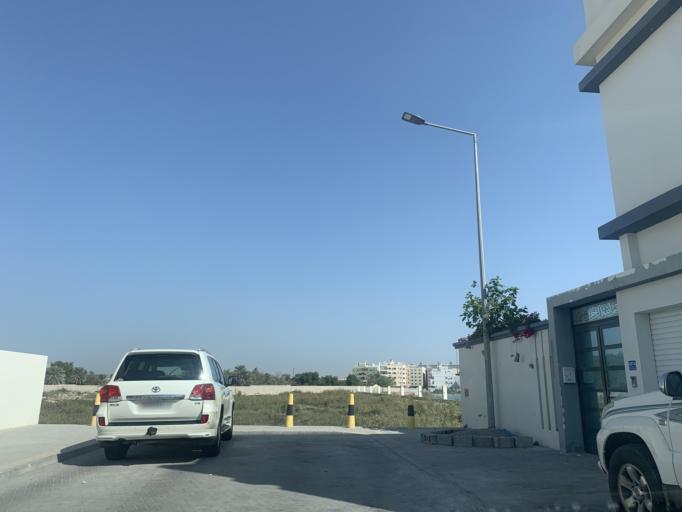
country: BH
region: Central Governorate
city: Madinat Hamad
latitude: 26.1340
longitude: 50.4834
